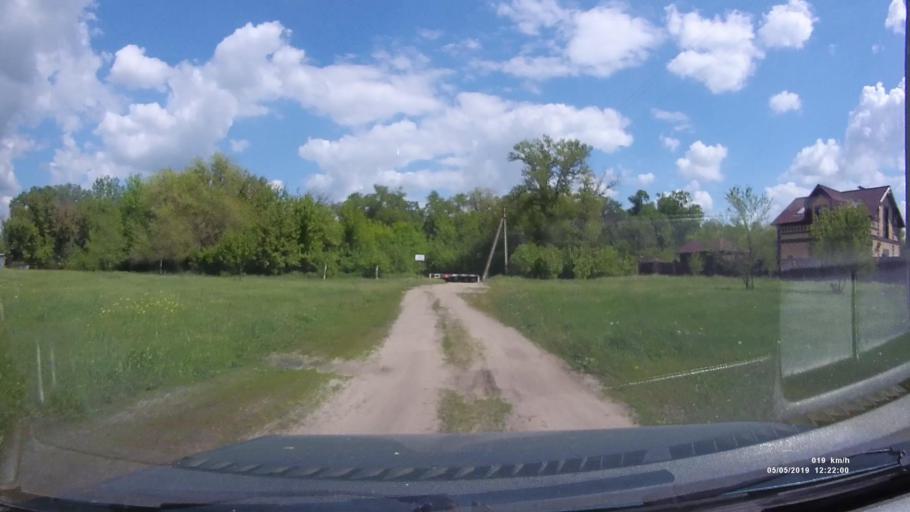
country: RU
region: Rostov
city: Konstantinovsk
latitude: 47.7555
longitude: 41.0399
